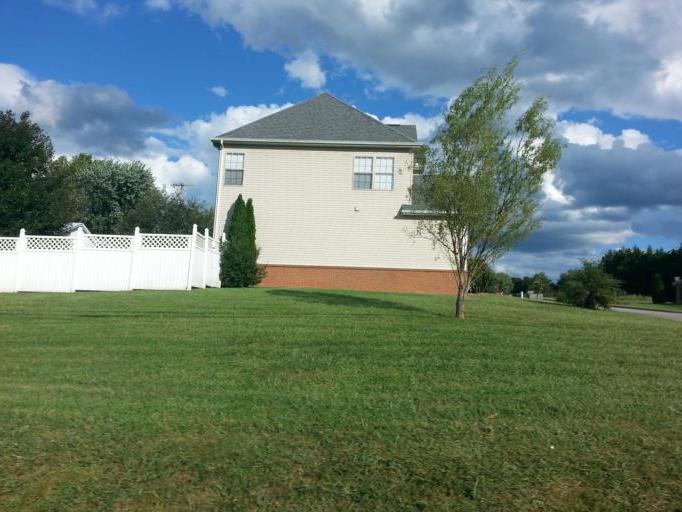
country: US
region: Tennessee
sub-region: Knox County
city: Mascot
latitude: 36.0898
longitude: -83.8193
